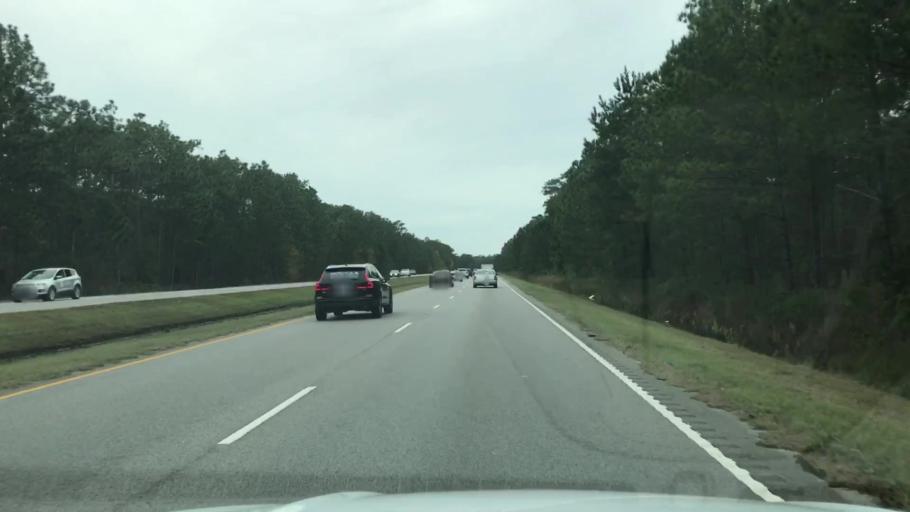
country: US
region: South Carolina
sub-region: Georgetown County
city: Georgetown
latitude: 33.4102
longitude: -79.1917
